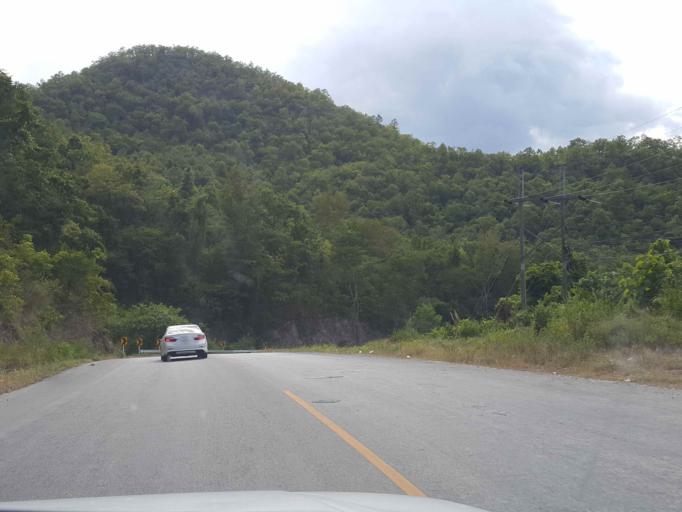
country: TH
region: Lampang
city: Thoen
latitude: 17.6414
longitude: 99.3046
